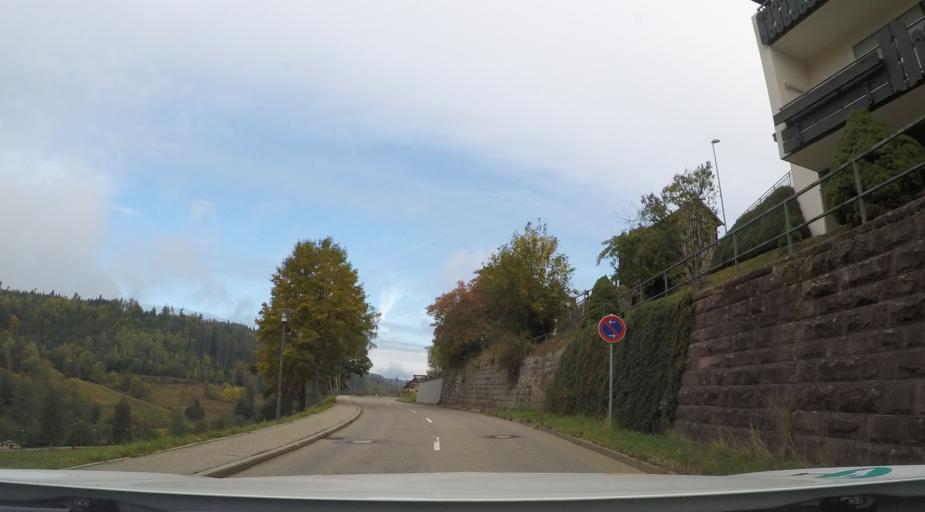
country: DE
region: Baden-Wuerttemberg
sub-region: Karlsruhe Region
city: Baiersbronn
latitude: 48.5339
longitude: 8.3607
